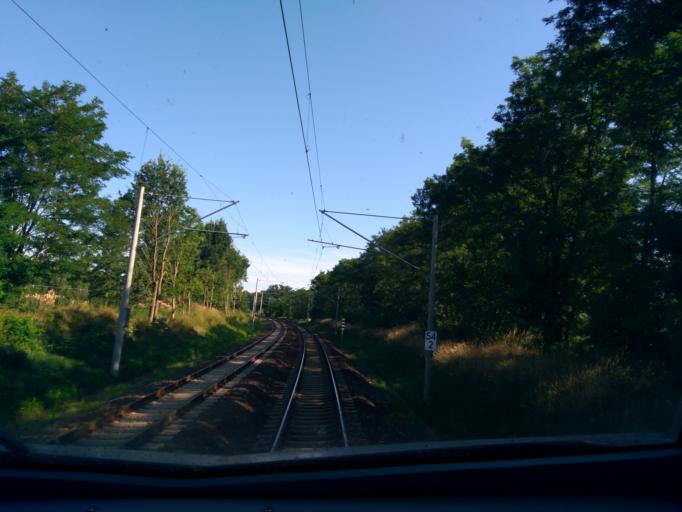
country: DE
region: Brandenburg
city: Halbe
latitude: 52.0787
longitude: 13.7267
